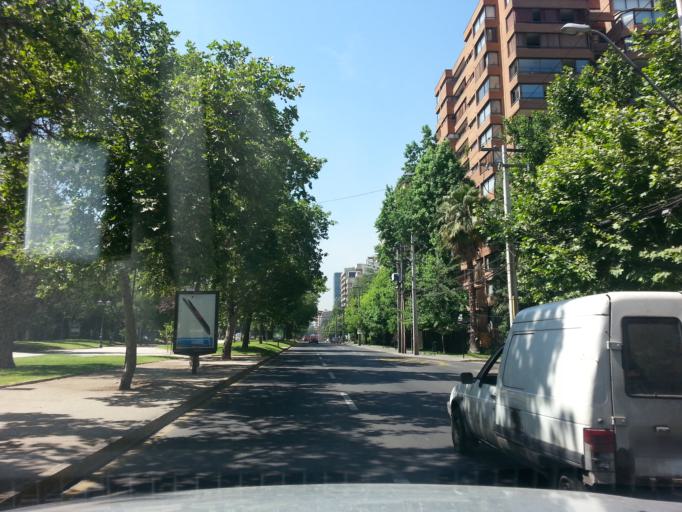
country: CL
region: Santiago Metropolitan
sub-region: Provincia de Santiago
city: Villa Presidente Frei, Nunoa, Santiago, Chile
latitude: -33.3992
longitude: -70.5879
